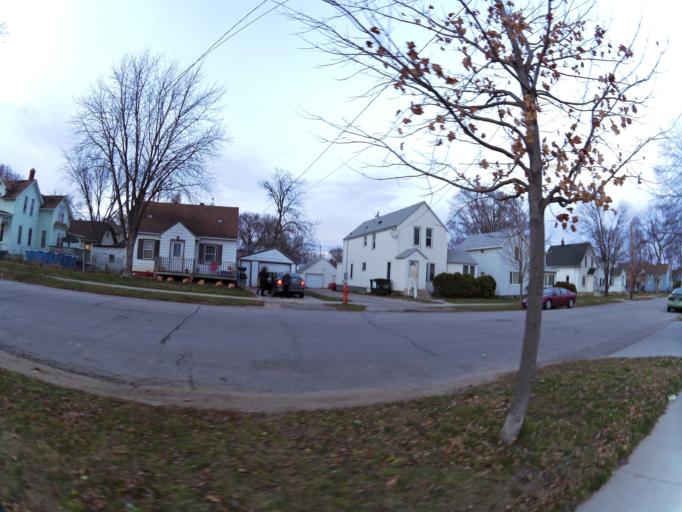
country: US
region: Minnesota
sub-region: Olmsted County
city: Rochester
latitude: 44.0322
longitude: -92.4649
